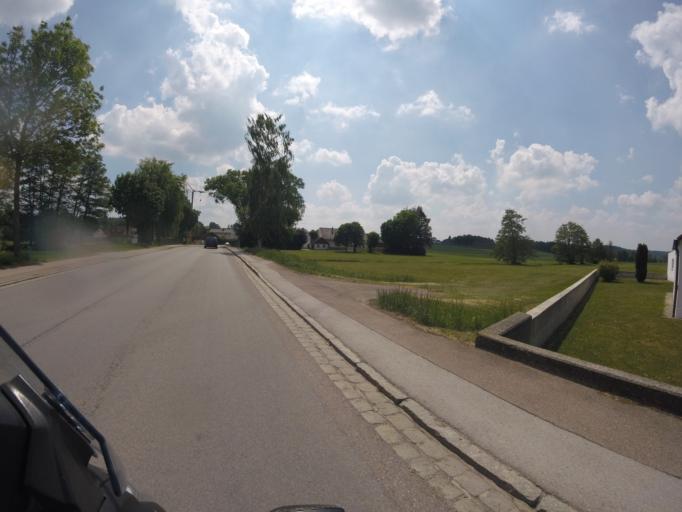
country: DE
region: Bavaria
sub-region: Upper Bavaria
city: Scheyern
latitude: 48.5176
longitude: 11.4629
